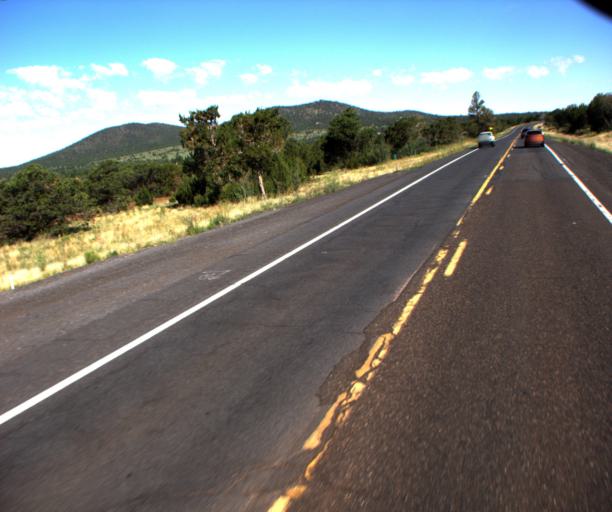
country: US
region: Arizona
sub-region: Coconino County
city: Williams
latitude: 35.3399
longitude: -112.1630
